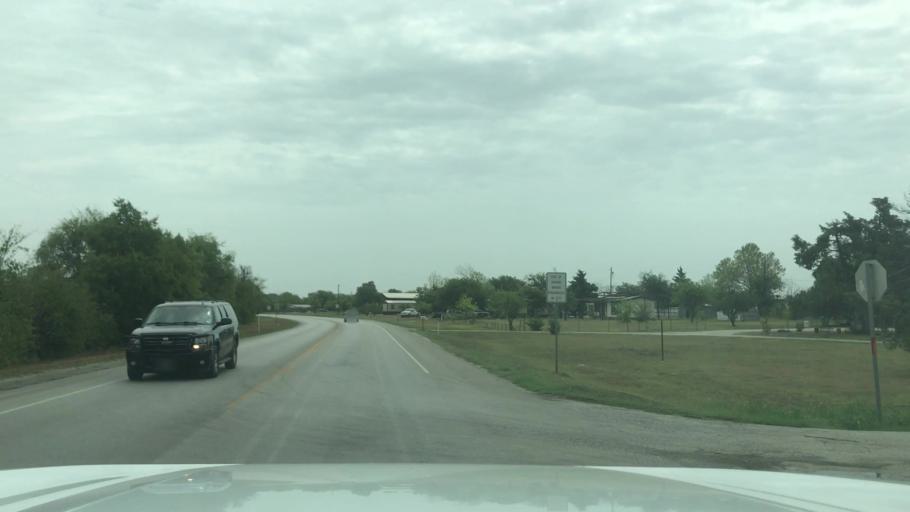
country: US
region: Texas
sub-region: Erath County
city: Dublin
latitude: 32.0894
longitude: -98.3589
